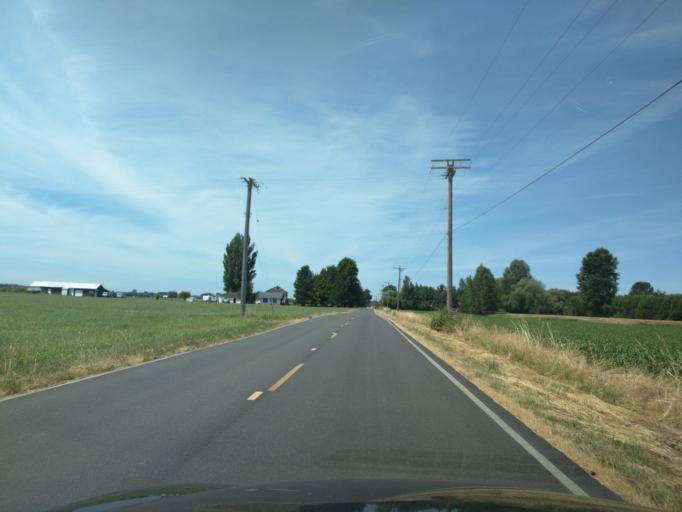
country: US
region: Washington
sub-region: Whatcom County
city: Lynden
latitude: 48.9349
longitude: -122.4244
